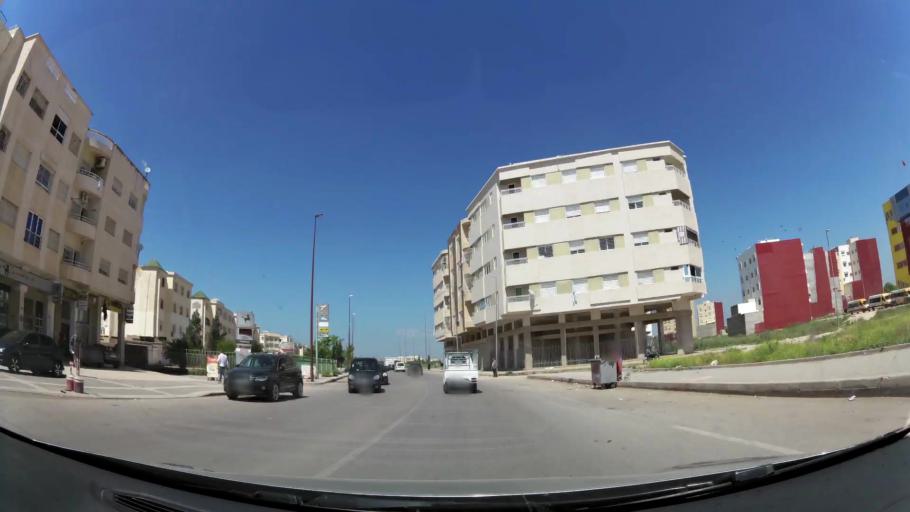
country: MA
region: Fes-Boulemane
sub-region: Fes
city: Fes
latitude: 34.0102
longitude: -5.0243
